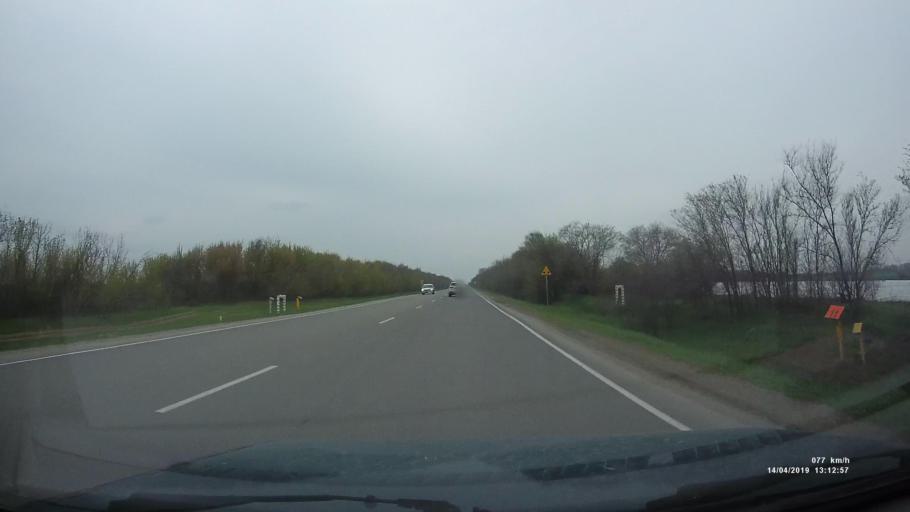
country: RU
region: Rostov
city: Kuleshovka
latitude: 47.0999
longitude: 39.6309
